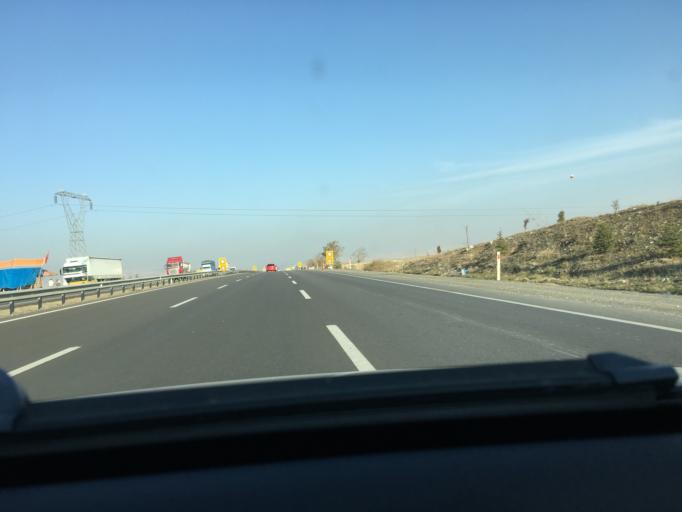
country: TR
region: Ankara
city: Temelli
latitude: 39.7387
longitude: 32.3975
